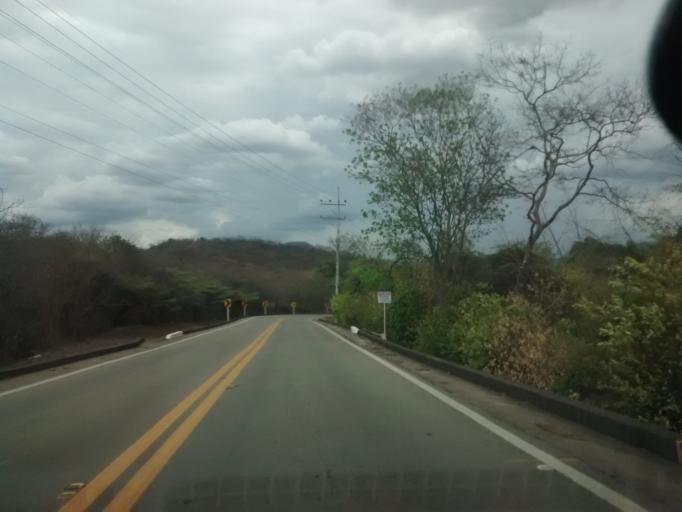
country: CO
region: Cundinamarca
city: Tocaima
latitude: 4.4334
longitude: -74.6876
